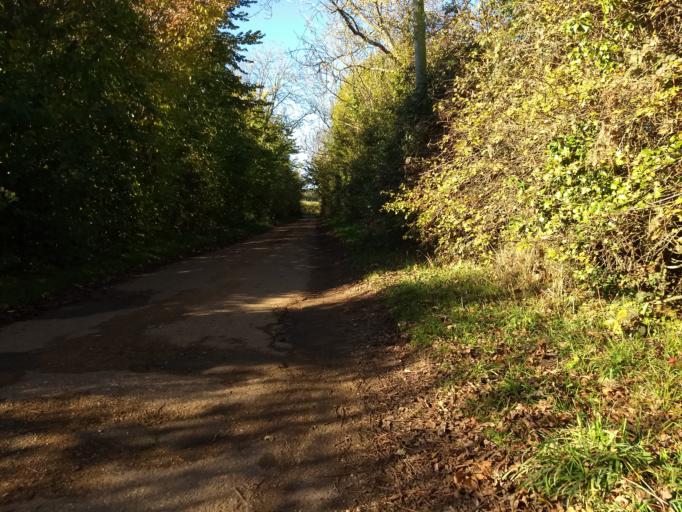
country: GB
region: England
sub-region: Isle of Wight
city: Newport
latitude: 50.6673
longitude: -1.2788
